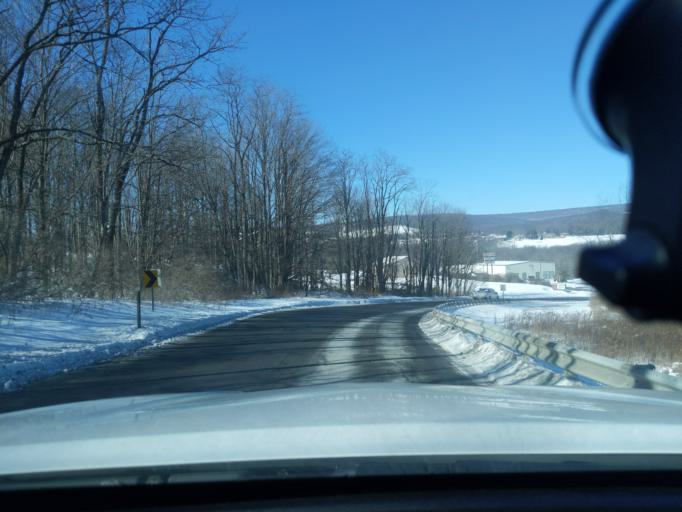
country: US
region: Maryland
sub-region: Allegany County
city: Frostburg
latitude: 39.6342
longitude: -78.9270
